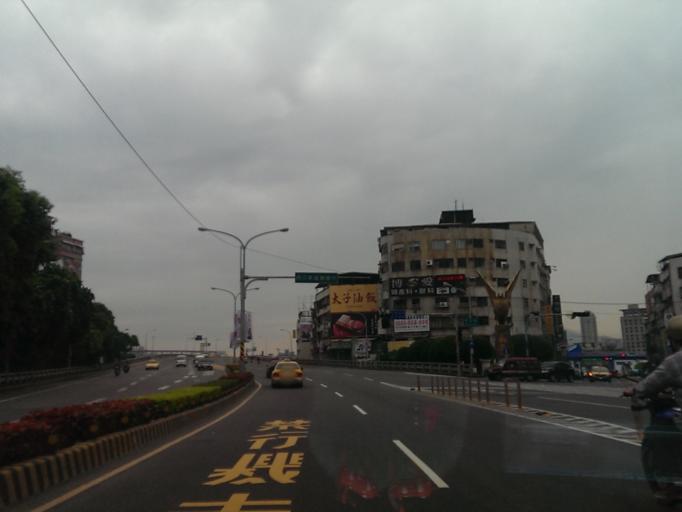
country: TW
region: Taipei
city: Taipei
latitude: 25.0163
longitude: 121.5162
